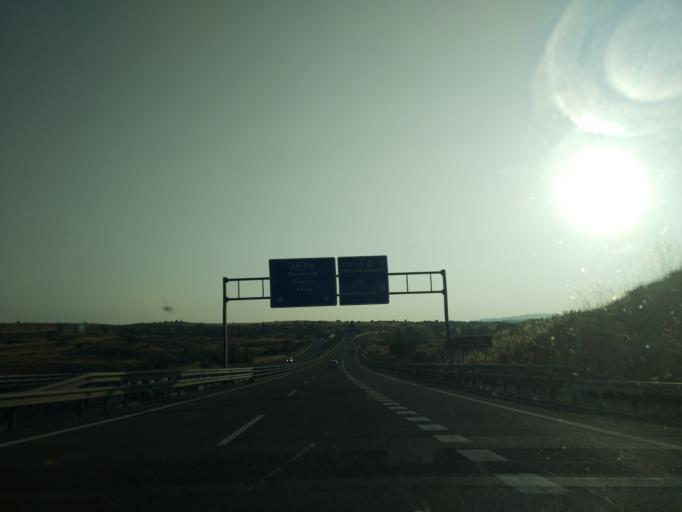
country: ES
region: Castille and Leon
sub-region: Provincia de Avila
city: Avila
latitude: 40.6713
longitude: -4.7077
